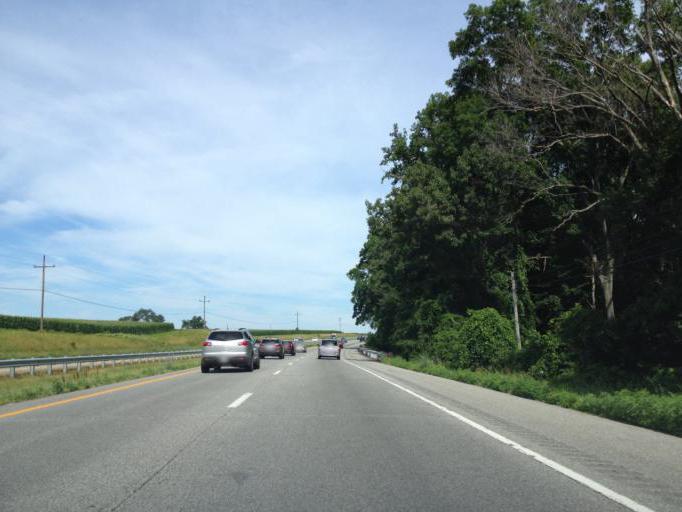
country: US
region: Maryland
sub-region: Queen Anne's County
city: Centreville
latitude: 38.9658
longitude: -76.1113
